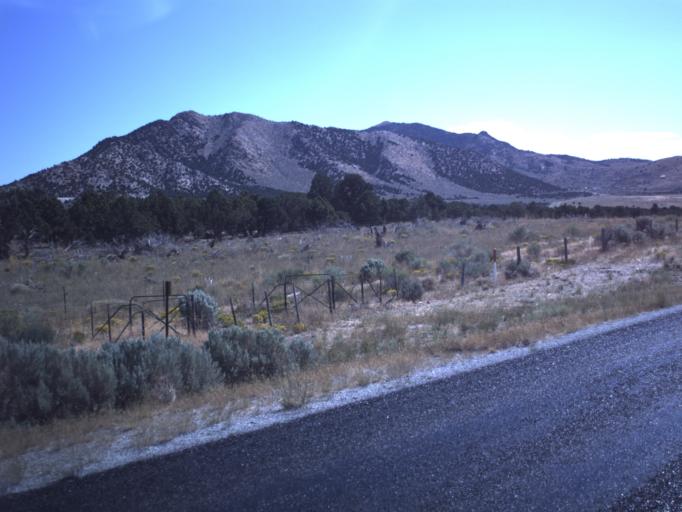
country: US
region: Utah
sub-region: Utah County
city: Genola
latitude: 39.9316
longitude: -112.1689
